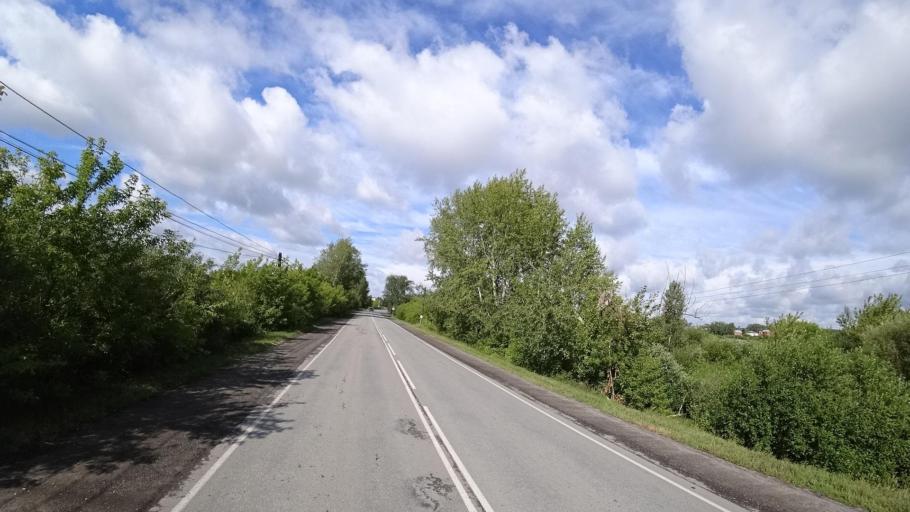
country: RU
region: Sverdlovsk
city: Kamyshlov
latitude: 56.8371
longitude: 62.6989
